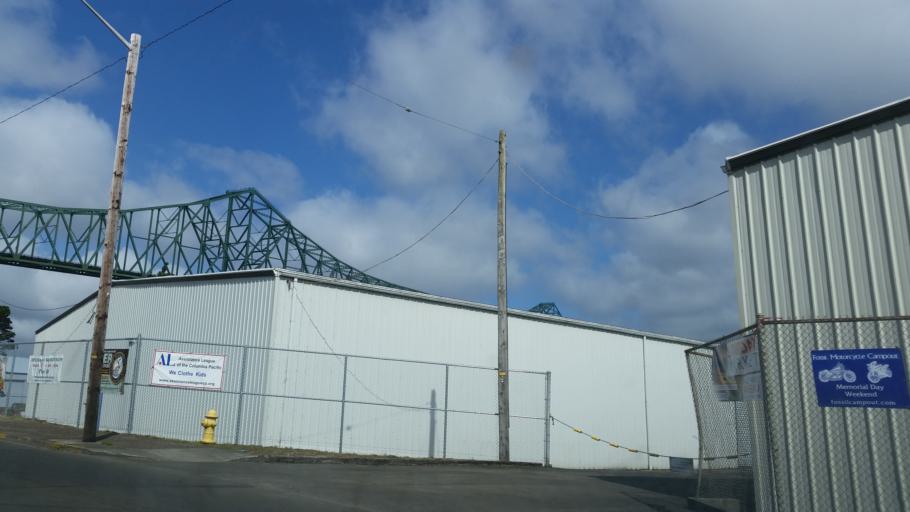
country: US
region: Oregon
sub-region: Clatsop County
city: Astoria
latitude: 46.1905
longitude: -123.8457
